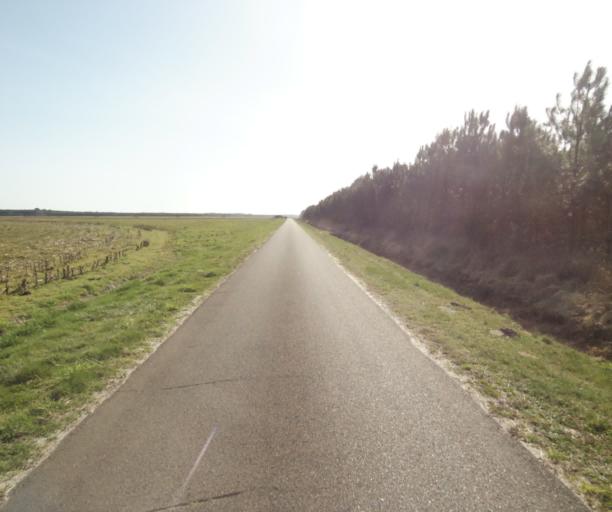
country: FR
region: Aquitaine
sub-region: Departement des Landes
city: Roquefort
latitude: 44.1775
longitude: -0.2517
